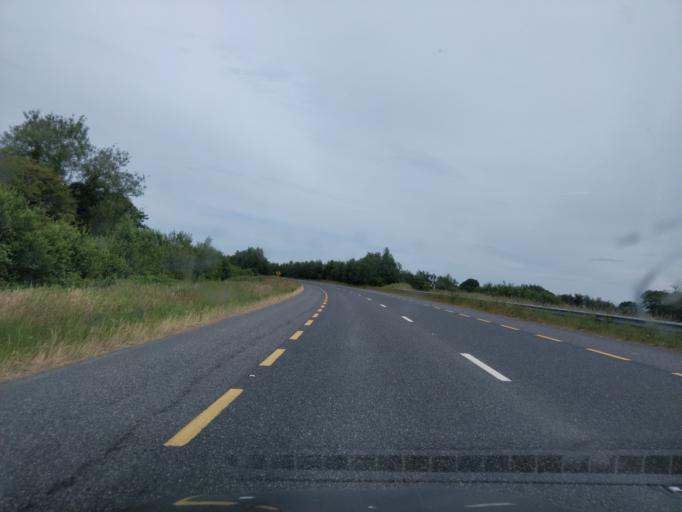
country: IE
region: Leinster
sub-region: Uibh Fhaili
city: Tullamore
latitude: 53.2516
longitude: -7.4898
